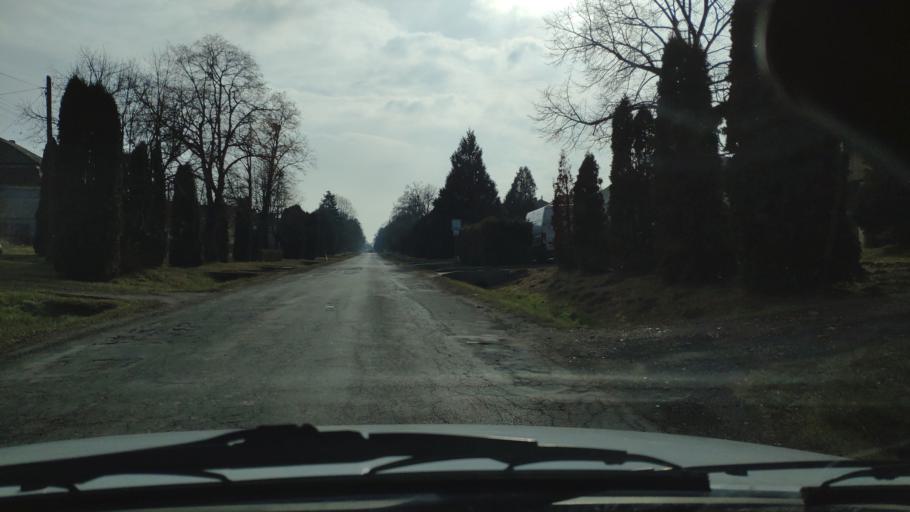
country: HU
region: Zala
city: Nagykanizsa
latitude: 46.4596
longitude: 16.9156
